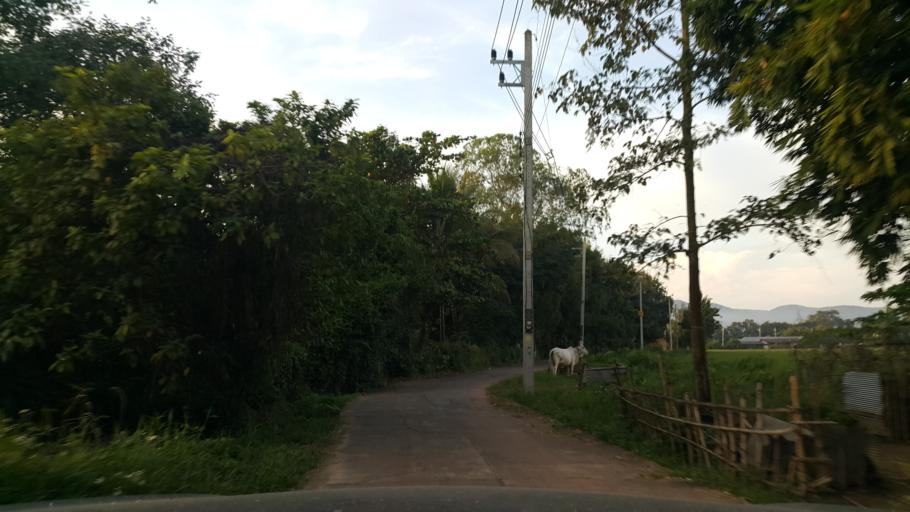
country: TH
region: Chiang Mai
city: San Sai
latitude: 18.8875
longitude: 99.0852
